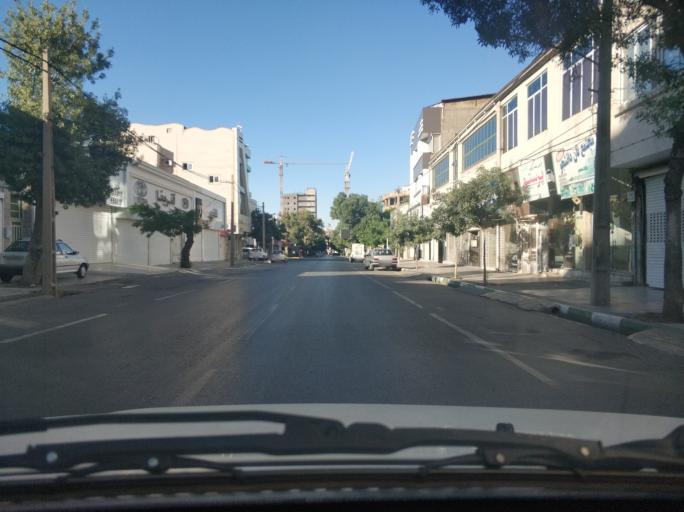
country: IR
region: Razavi Khorasan
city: Mashhad
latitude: 36.2791
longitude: 59.5965
